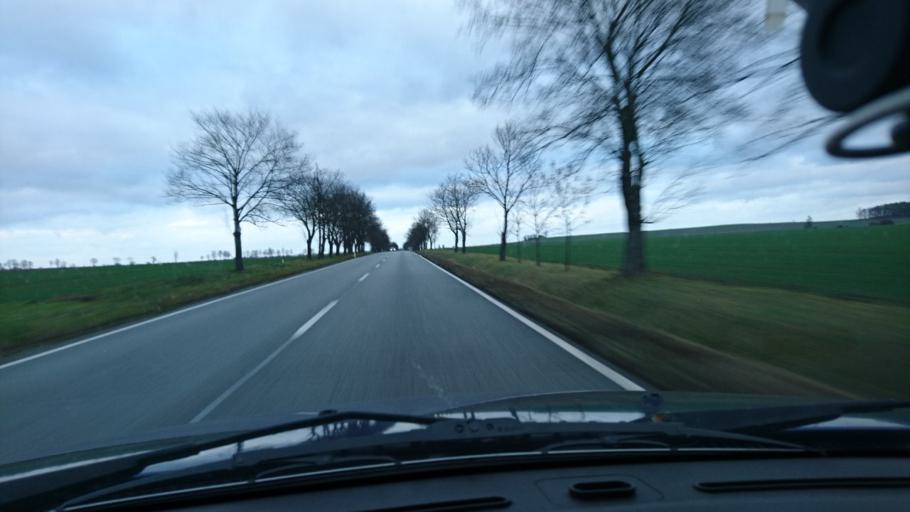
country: PL
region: Opole Voivodeship
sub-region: Powiat kluczborski
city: Byczyna
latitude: 51.0874
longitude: 18.1995
